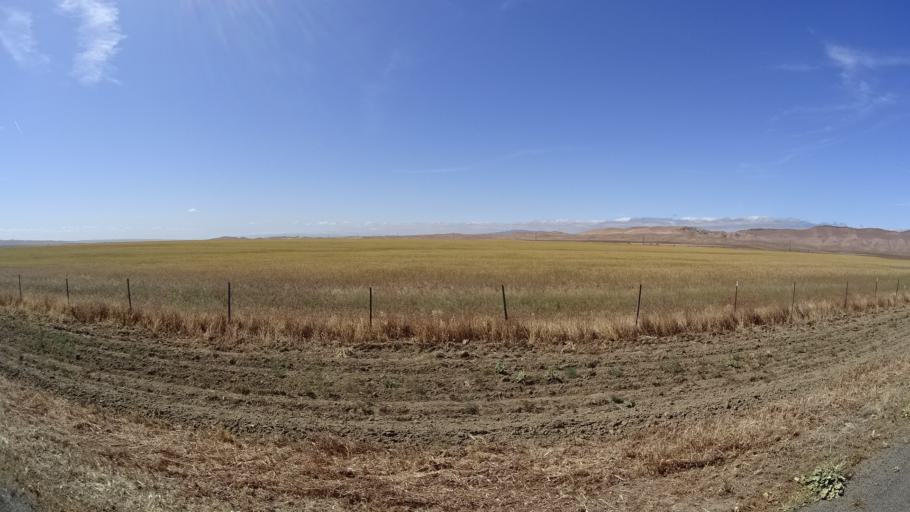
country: US
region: California
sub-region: Kings County
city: Avenal
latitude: 35.9351
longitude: -120.0795
